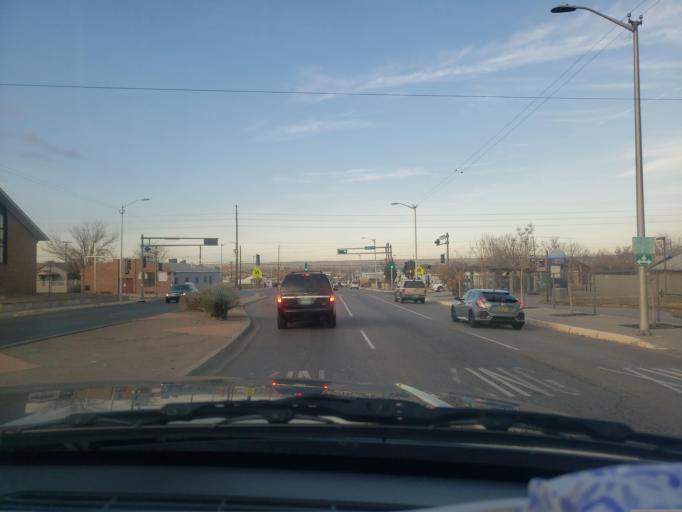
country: US
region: New Mexico
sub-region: Bernalillo County
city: Albuquerque
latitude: 35.0698
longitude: -106.6423
